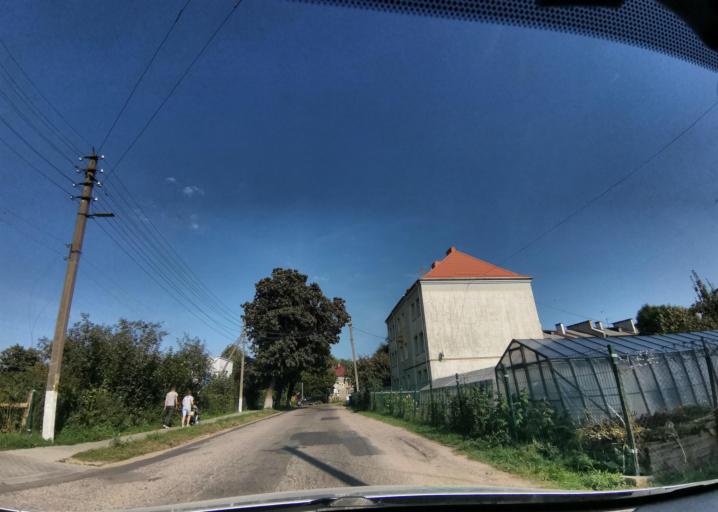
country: RU
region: Kaliningrad
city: Neman
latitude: 55.0328
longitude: 22.0411
